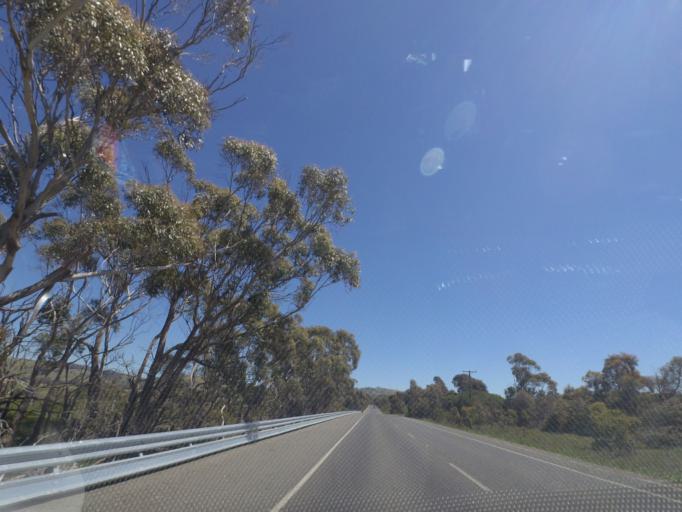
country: AU
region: Victoria
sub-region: Hume
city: Sunbury
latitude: -37.3048
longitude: 144.8346
